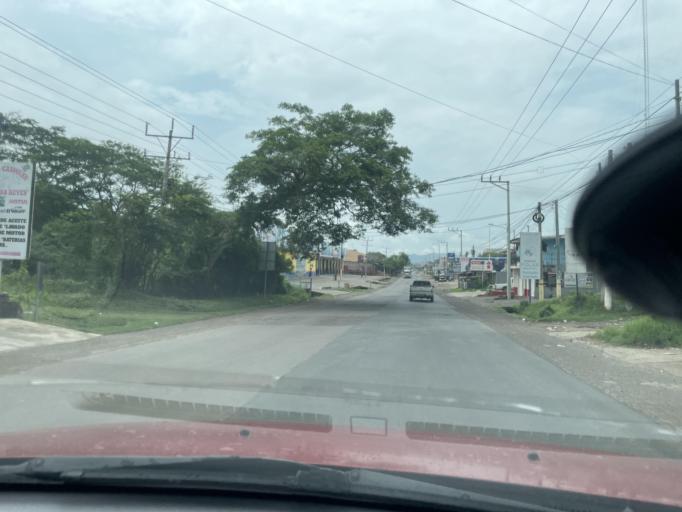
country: SV
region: La Union
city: Santa Rosa de Lima
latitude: 13.6280
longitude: -87.8772
